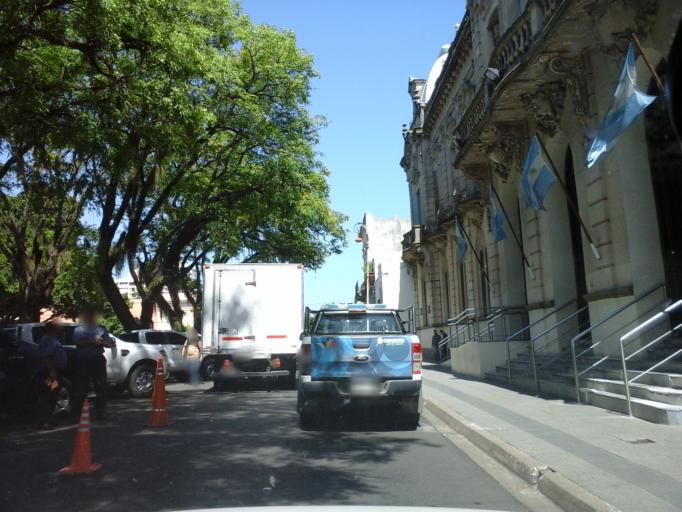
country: AR
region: Corrientes
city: Corrientes
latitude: -27.4628
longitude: -58.8392
